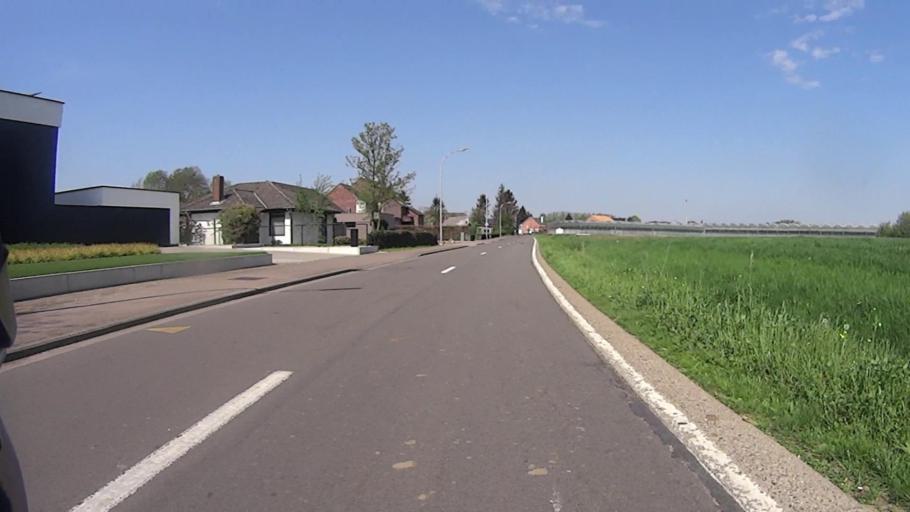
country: BE
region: Flanders
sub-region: Provincie Antwerpen
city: Sint-Amands
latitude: 51.0493
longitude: 4.2316
